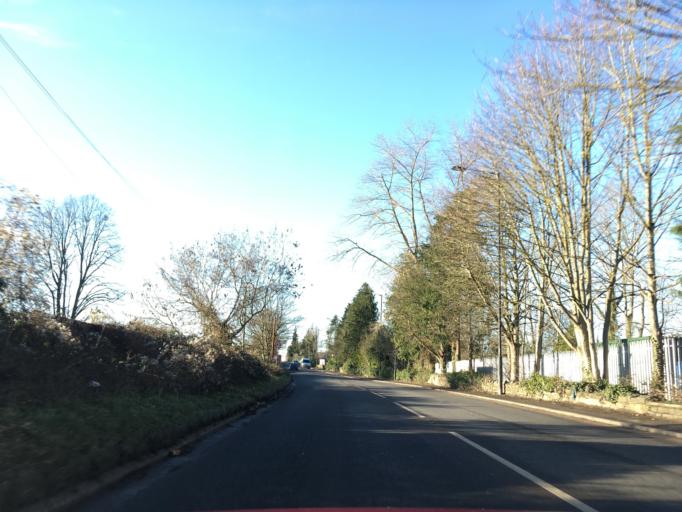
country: GB
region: England
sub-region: Bath and North East Somerset
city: Corston
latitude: 51.3878
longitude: -2.4078
